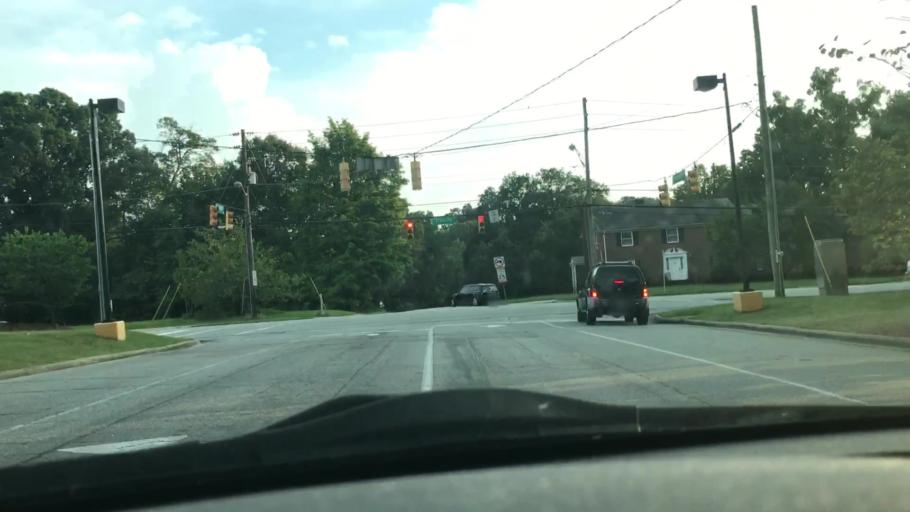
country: US
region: North Carolina
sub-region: Guilford County
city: Greensboro
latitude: 36.0852
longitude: -79.8349
